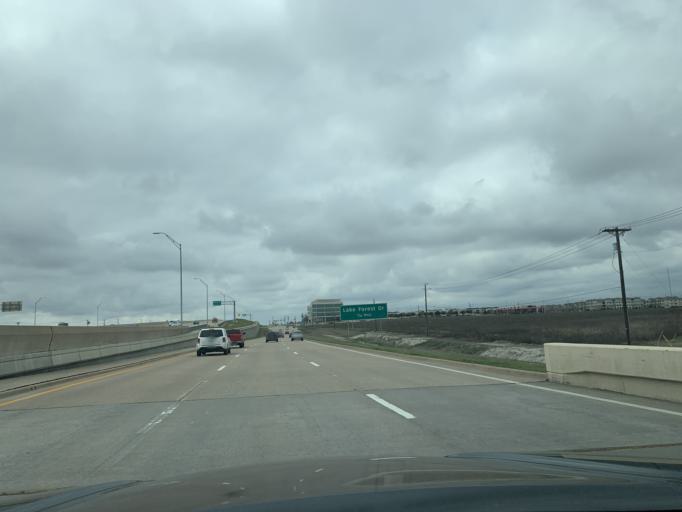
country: US
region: Texas
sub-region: Collin County
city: Fairview
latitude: 33.1471
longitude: -96.6741
